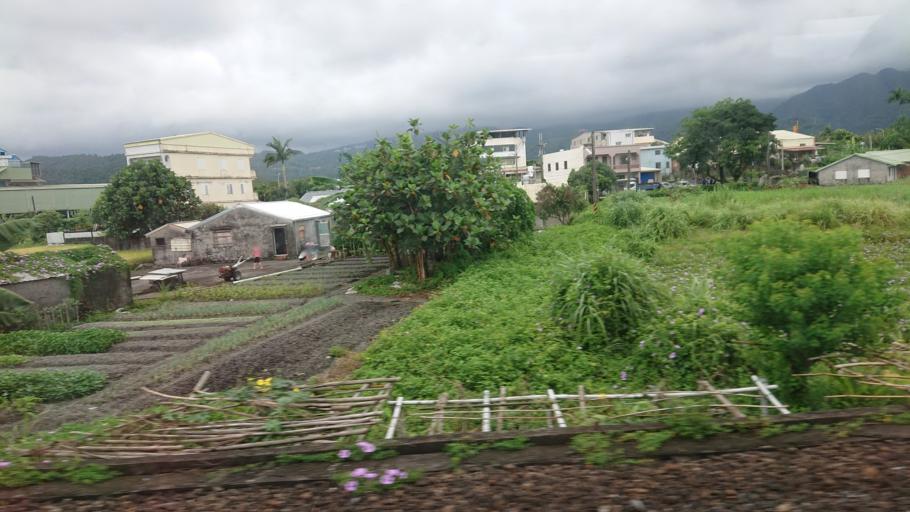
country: TW
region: Taiwan
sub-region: Yilan
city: Yilan
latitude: 24.8124
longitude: 121.7692
